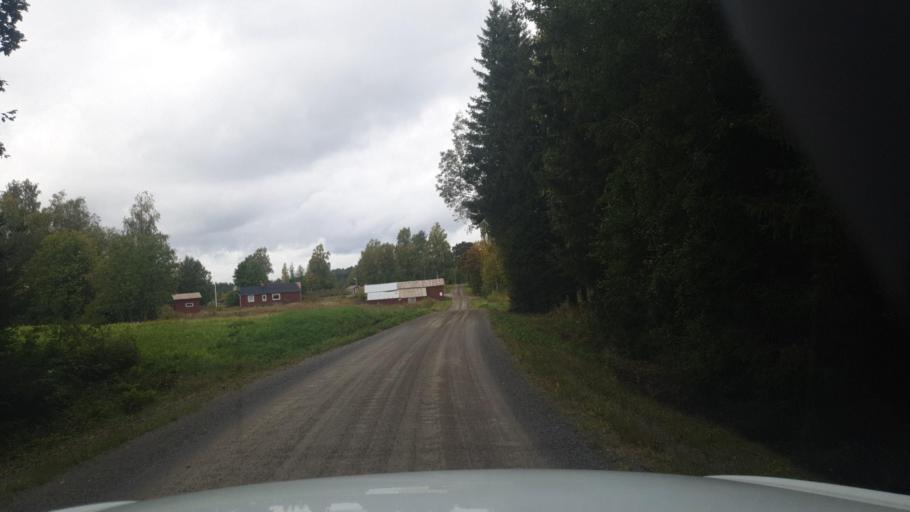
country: SE
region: Vaermland
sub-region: Torsby Kommun
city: Torsby
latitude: 59.9340
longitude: 12.8202
